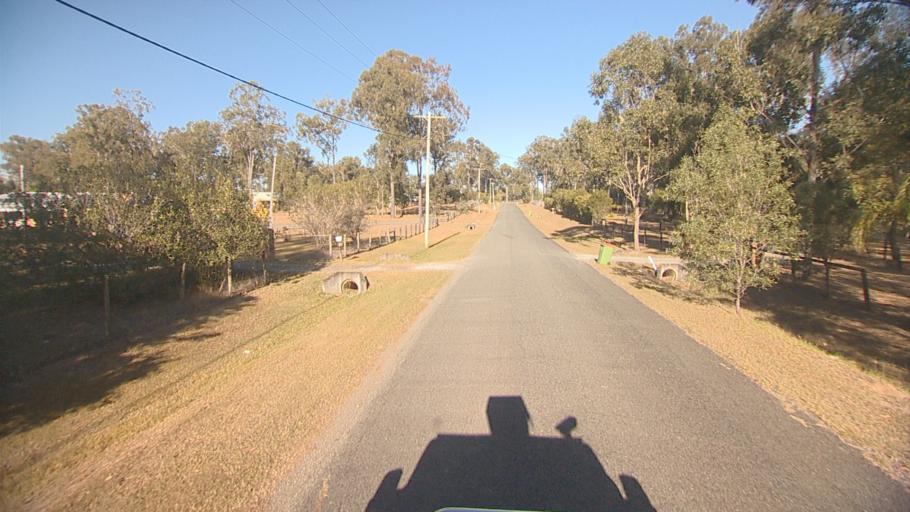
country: AU
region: Queensland
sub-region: Logan
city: Cedar Vale
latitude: -27.8378
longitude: 153.0142
